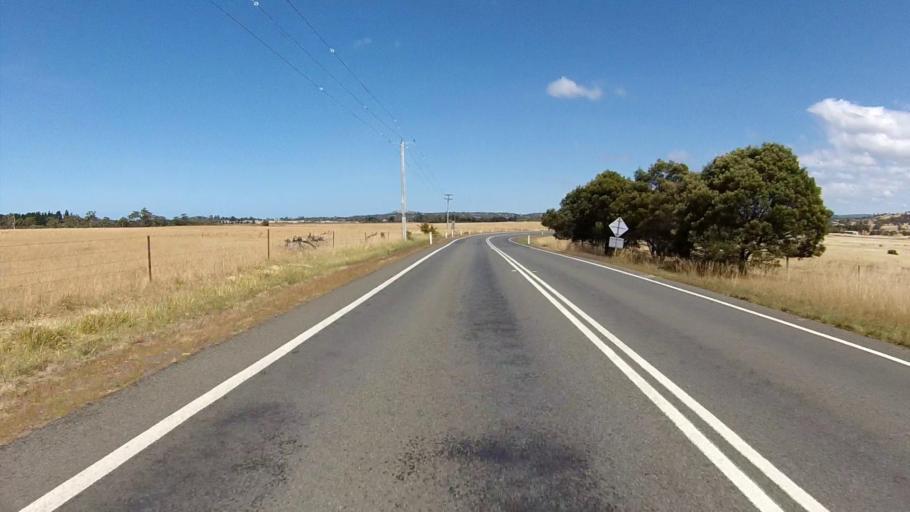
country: AU
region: Tasmania
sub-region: Break O'Day
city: St Helens
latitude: -42.1002
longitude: 148.0628
